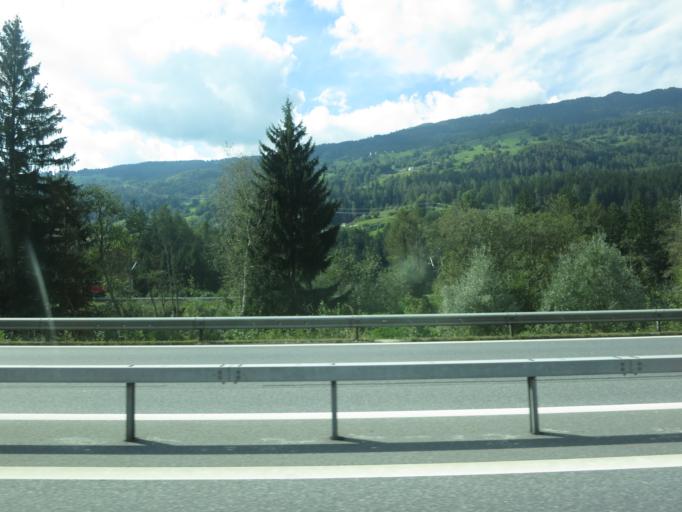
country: CH
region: Grisons
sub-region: Hinterrhein District
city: Cazis
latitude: 46.7462
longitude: 9.4313
